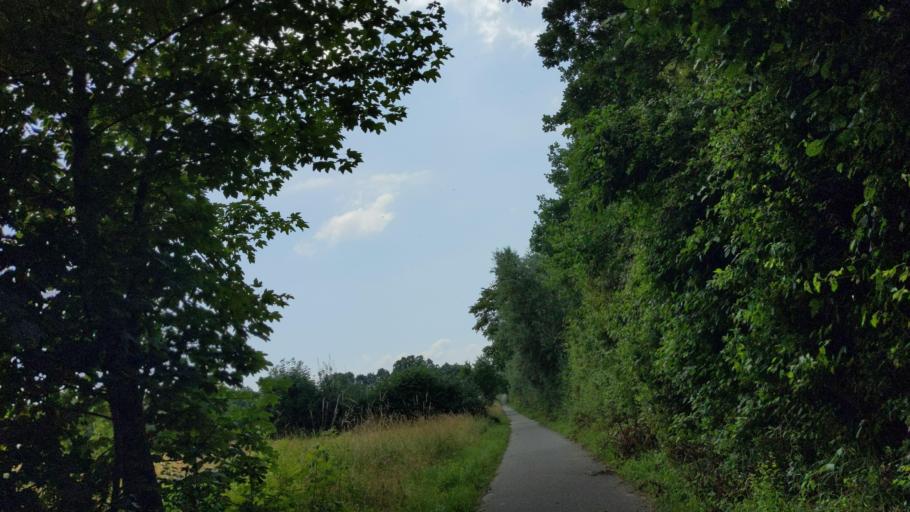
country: DE
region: Schleswig-Holstein
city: Altenkrempe
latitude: 54.1344
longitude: 10.8488
